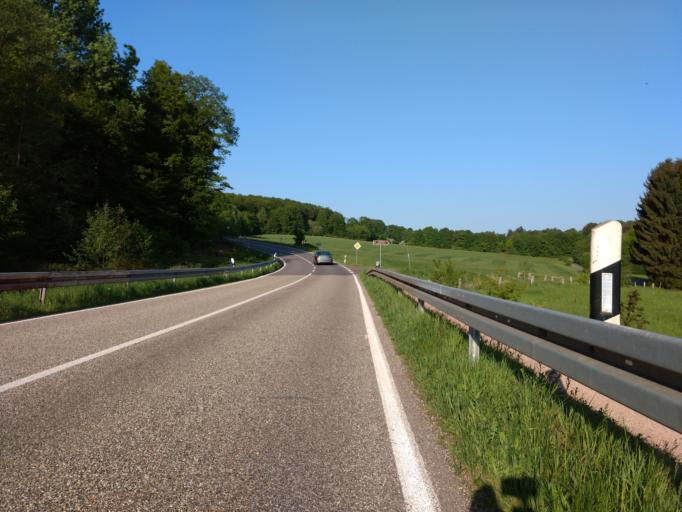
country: DE
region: Saarland
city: Saarwellingen
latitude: 49.3658
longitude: 6.8277
